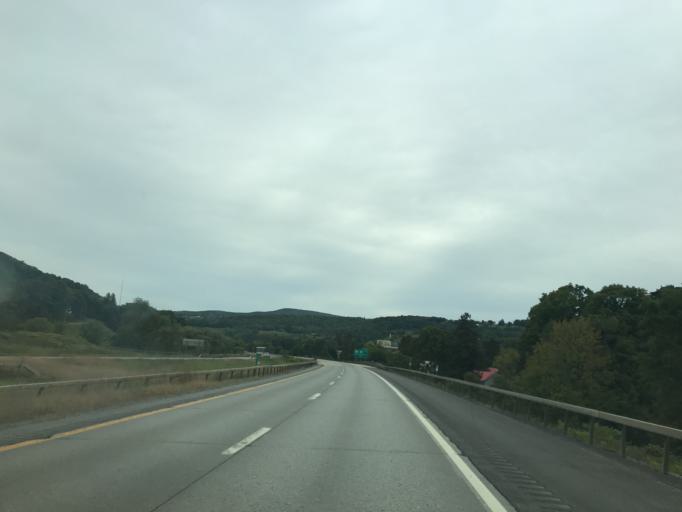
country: US
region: New York
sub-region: Schoharie County
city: Cobleskill
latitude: 42.6382
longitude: -74.5722
